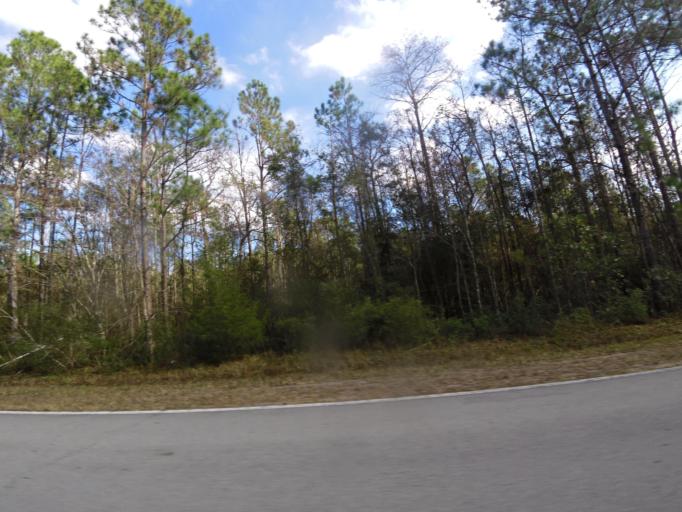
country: US
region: Florida
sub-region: Duval County
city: Baldwin
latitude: 30.1953
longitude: -81.9911
